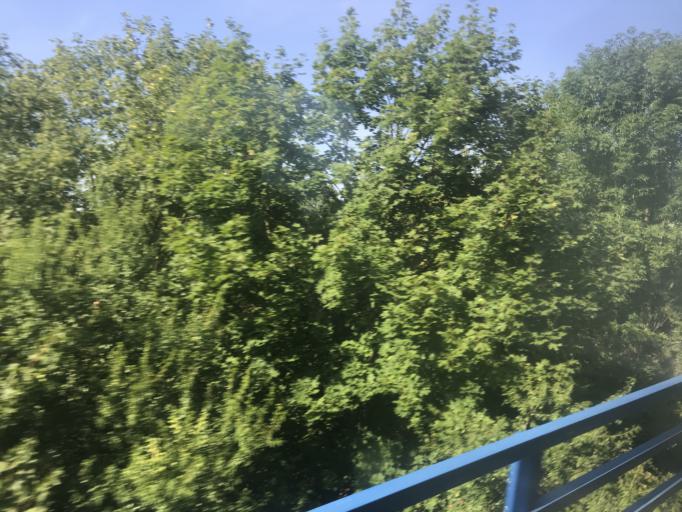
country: PL
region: West Pomeranian Voivodeship
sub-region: Szczecin
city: Szczecin
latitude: 53.3992
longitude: 14.5153
